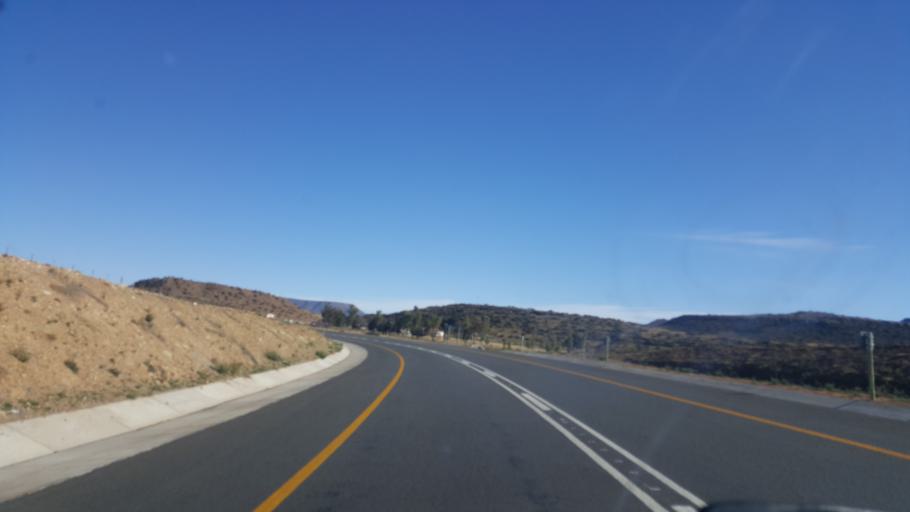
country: ZA
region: Eastern Cape
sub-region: Chris Hani District Municipality
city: Middelburg
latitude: -31.3769
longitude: 25.0338
